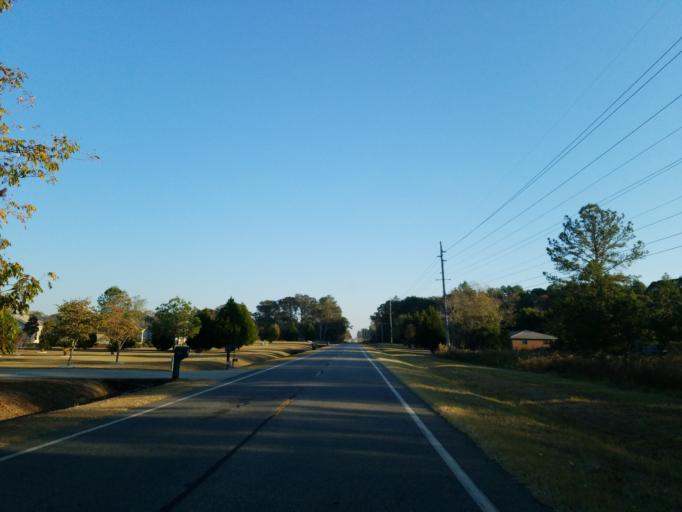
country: US
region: Georgia
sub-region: Crisp County
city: Cordele
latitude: 31.9313
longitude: -83.7270
